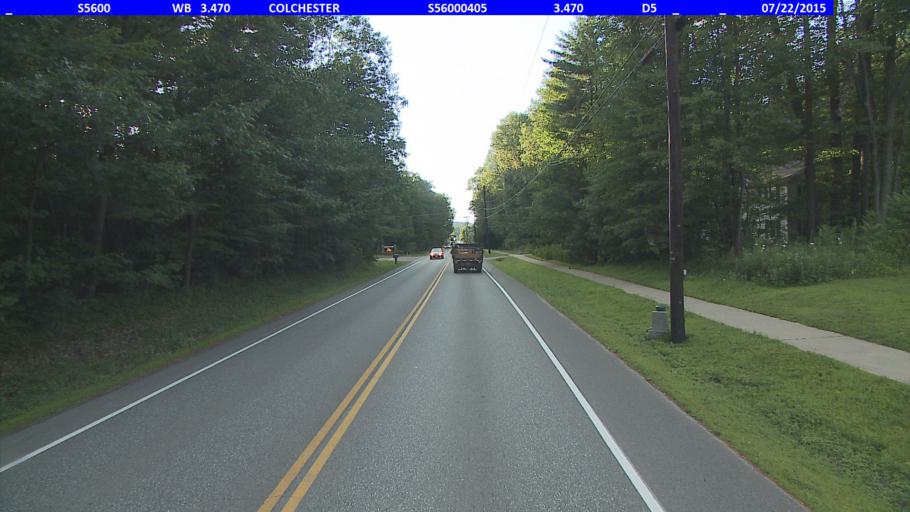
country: US
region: Vermont
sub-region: Chittenden County
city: Winooski
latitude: 44.5416
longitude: -73.2123
